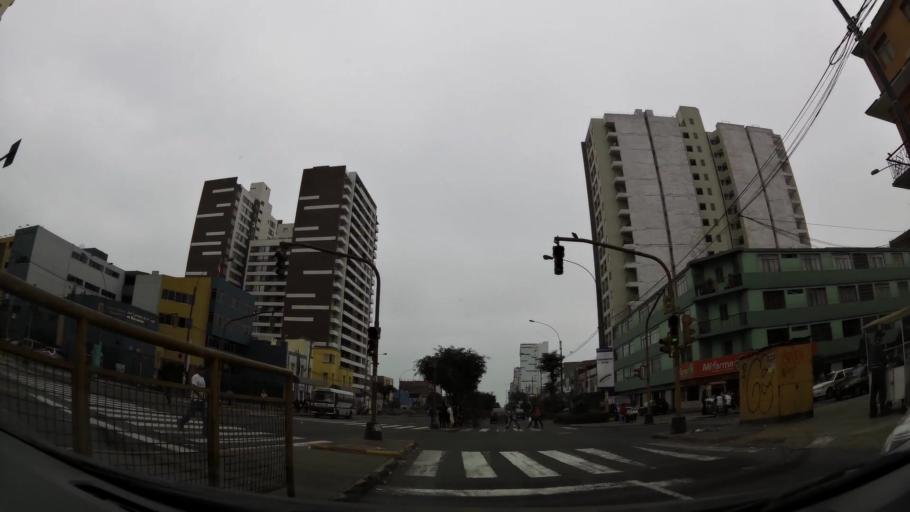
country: PE
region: Lima
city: Lima
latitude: -12.0690
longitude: -77.0489
